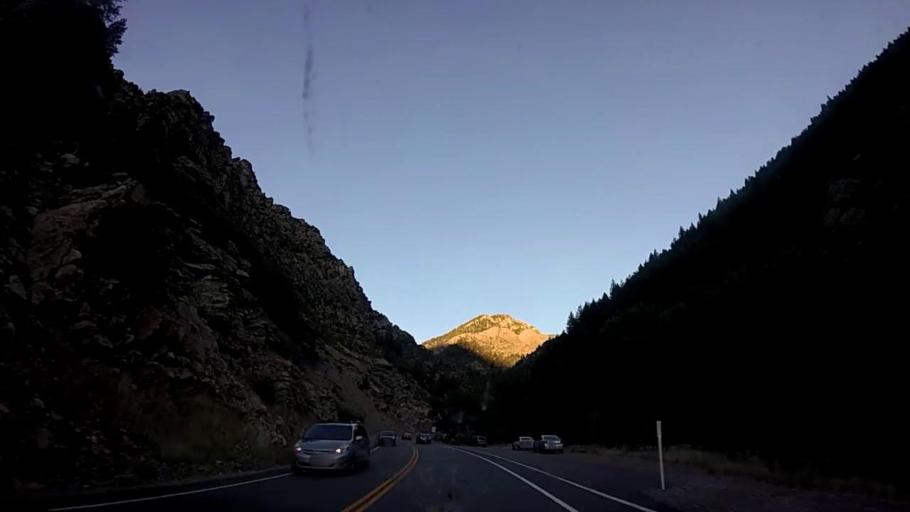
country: US
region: Utah
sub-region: Salt Lake County
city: Mount Olympus
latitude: 40.6340
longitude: -111.7107
